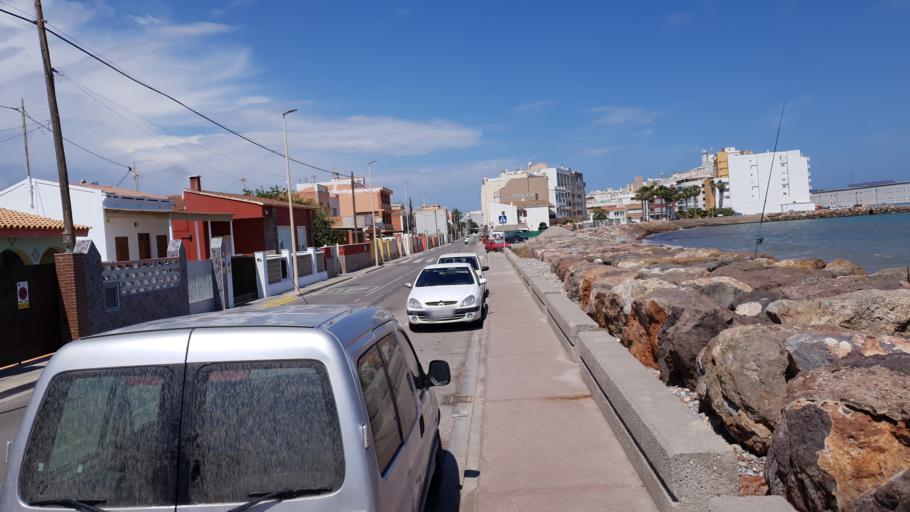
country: ES
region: Valencia
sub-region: Provincia de Castello
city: Burriana
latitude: 39.8617
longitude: -0.0798
